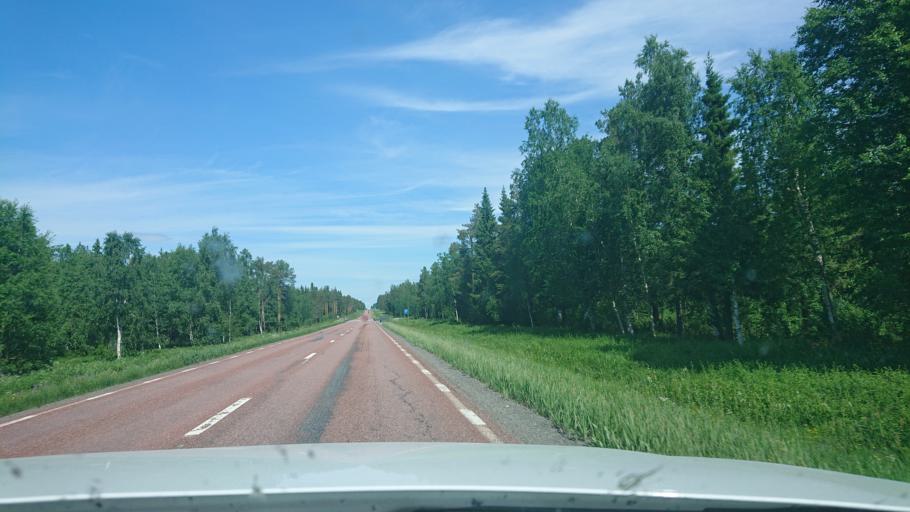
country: SE
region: Jaemtland
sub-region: Stroemsunds Kommun
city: Stroemsund
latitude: 63.7555
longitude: 15.4984
